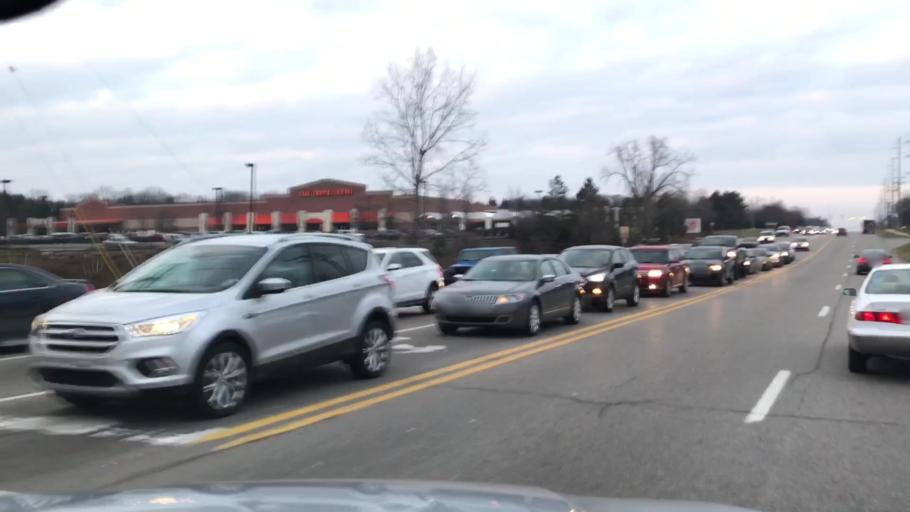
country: US
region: Michigan
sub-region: Wayne County
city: Northville
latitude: 42.4251
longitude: -83.4329
